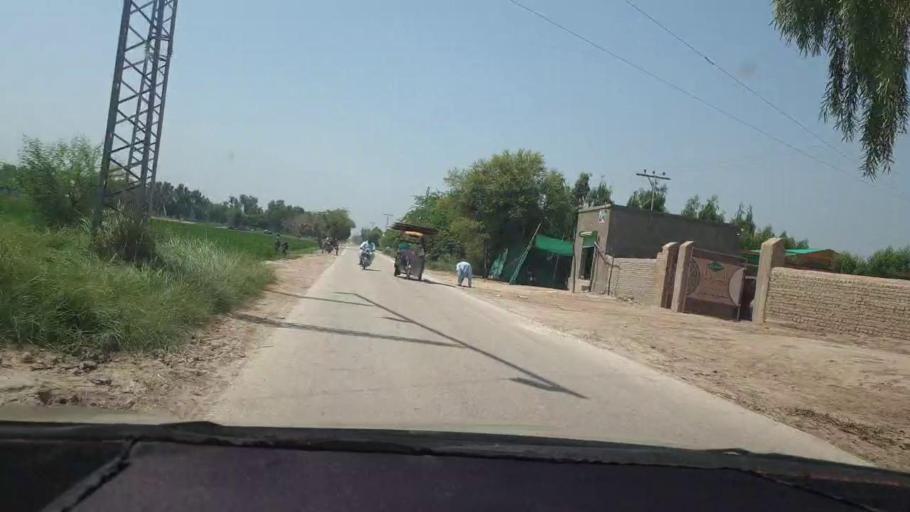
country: PK
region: Sindh
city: Kambar
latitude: 27.6000
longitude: 68.0274
